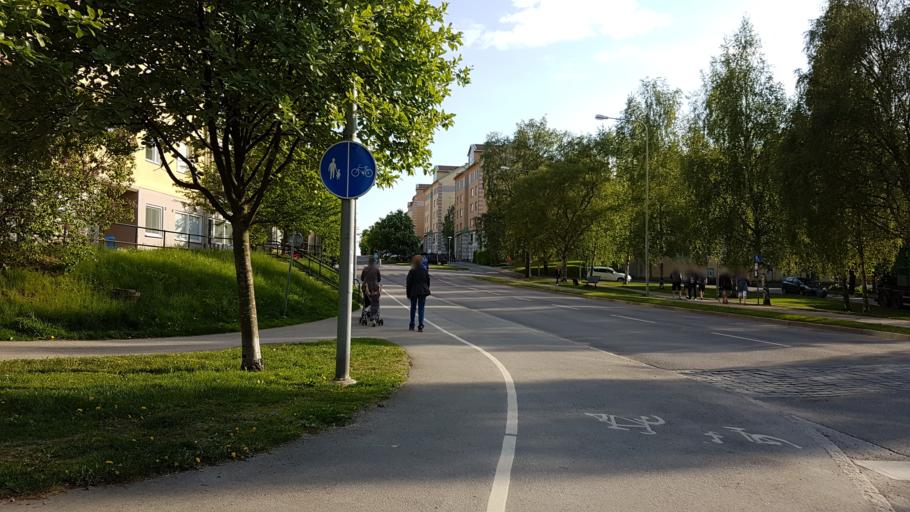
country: SE
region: Stockholm
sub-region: Sundbybergs Kommun
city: Sundbyberg
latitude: 59.3683
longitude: 17.9604
